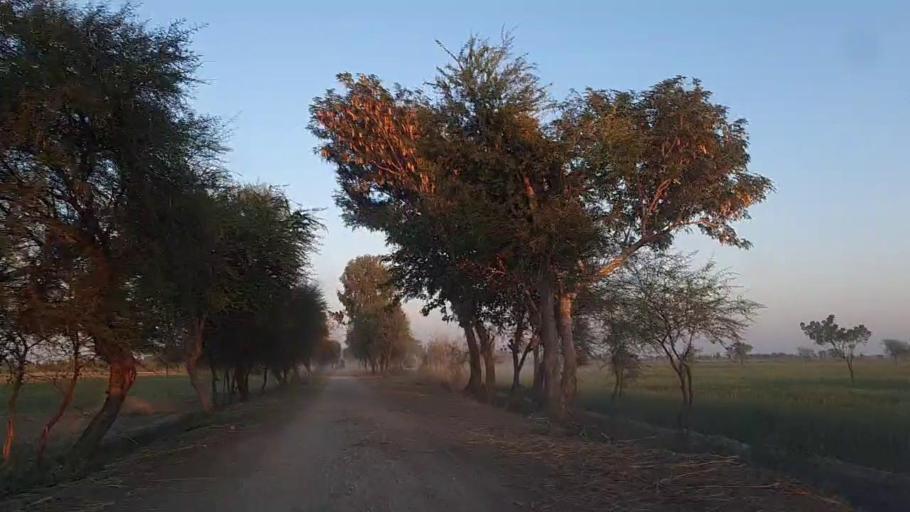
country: PK
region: Sindh
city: Samaro
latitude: 25.3182
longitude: 69.3638
